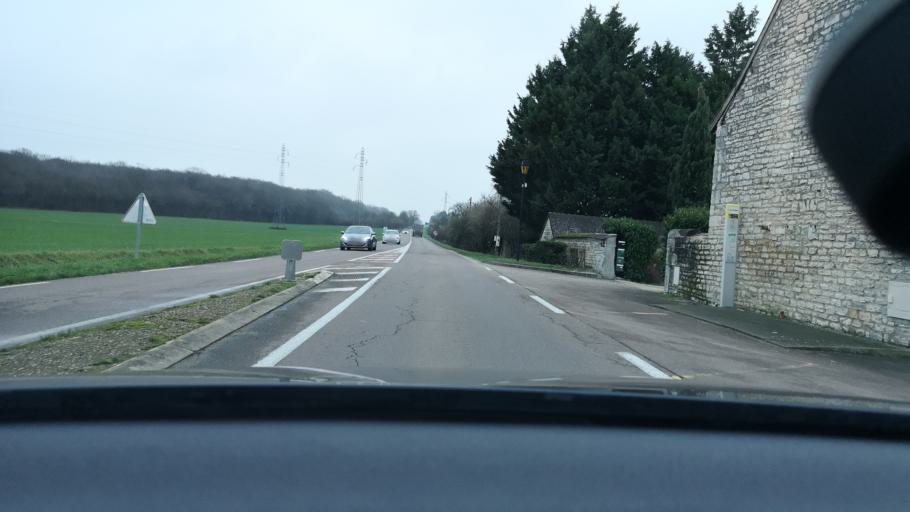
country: FR
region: Bourgogne
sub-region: Departement de Saone-et-Loire
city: Dracy-le-Fort
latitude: 46.8035
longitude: 4.7757
